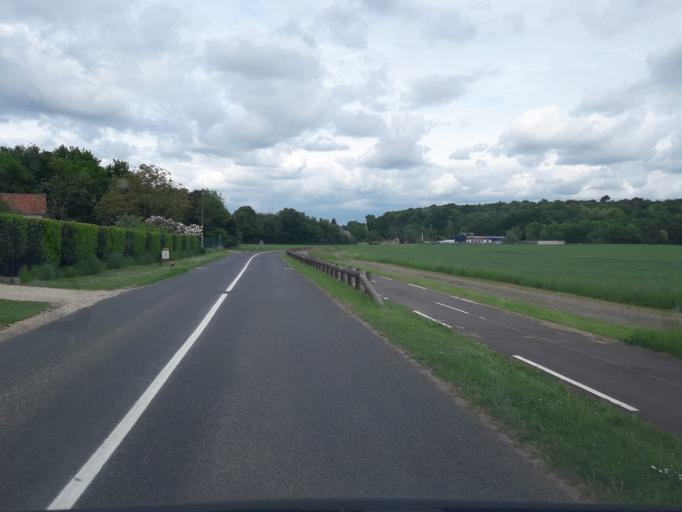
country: FR
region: Ile-de-France
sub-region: Departement de l'Essonne
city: Boissy-le-Cutte
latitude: 48.4514
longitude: 2.3095
